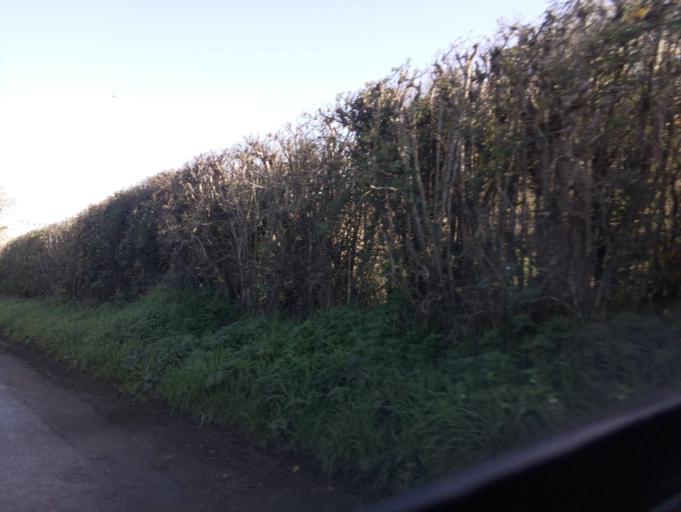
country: GB
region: England
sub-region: Somerset
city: Bruton
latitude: 51.0779
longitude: -2.4723
